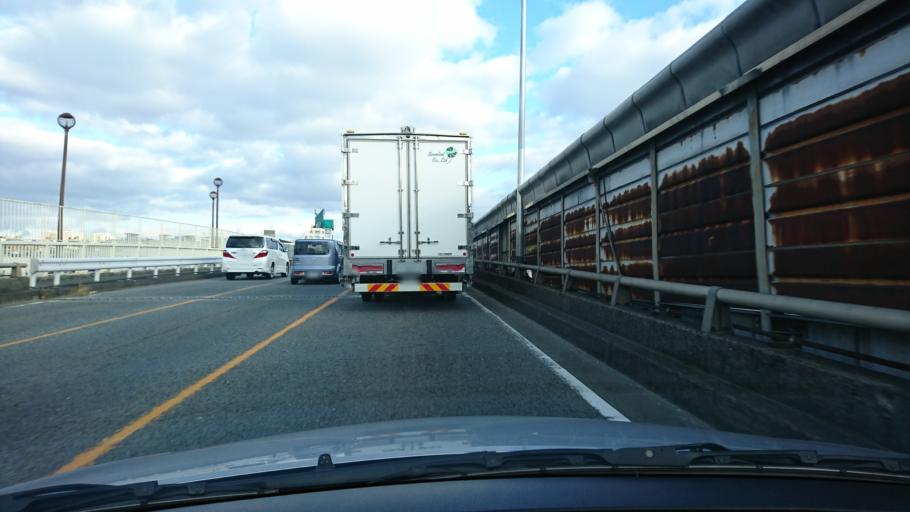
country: JP
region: Osaka
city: Ikeda
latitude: 34.8004
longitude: 135.4468
